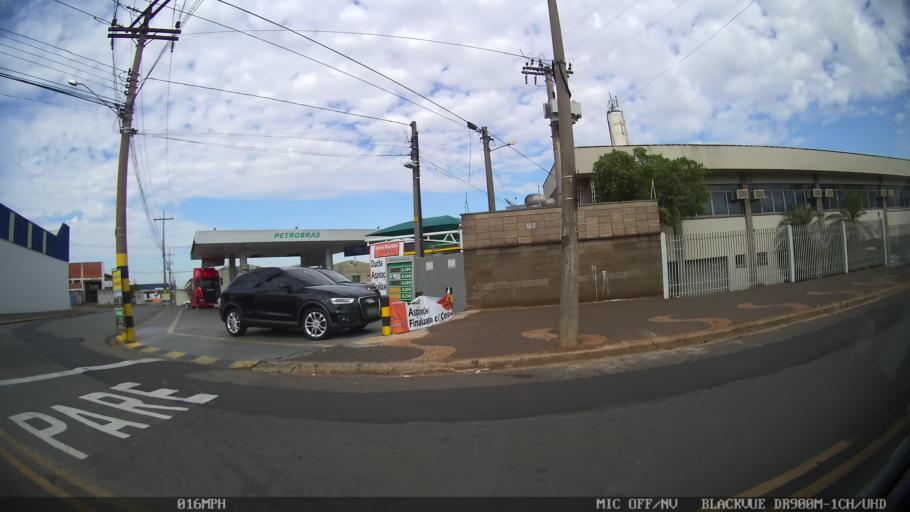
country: BR
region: Sao Paulo
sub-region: Americana
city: Americana
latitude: -22.7432
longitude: -47.3571
